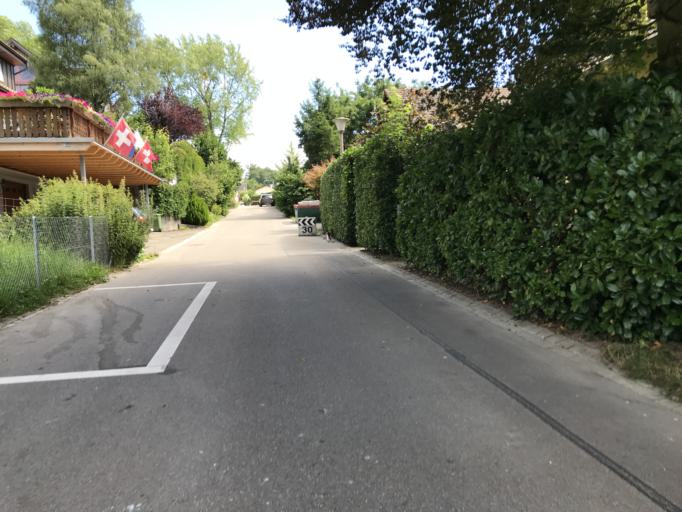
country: CH
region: Zurich
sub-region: Bezirk Winterthur
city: Neftenbach / Dorf Neftenbach
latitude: 47.5251
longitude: 8.6710
